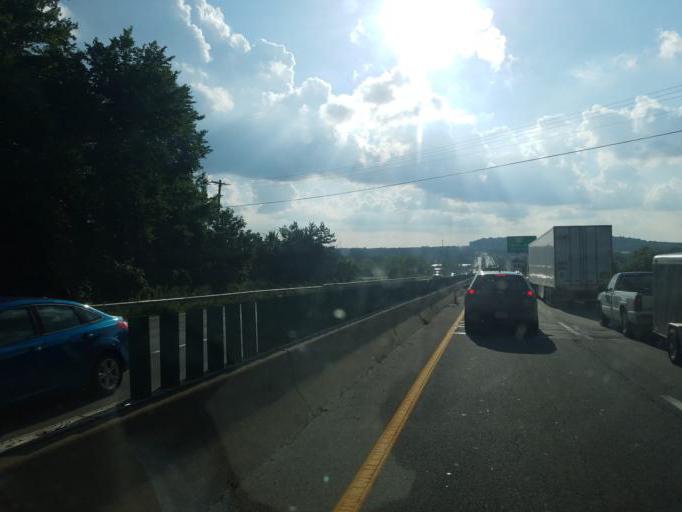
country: US
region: Ohio
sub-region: Richland County
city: Lincoln Heights
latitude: 40.7789
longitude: -82.5027
